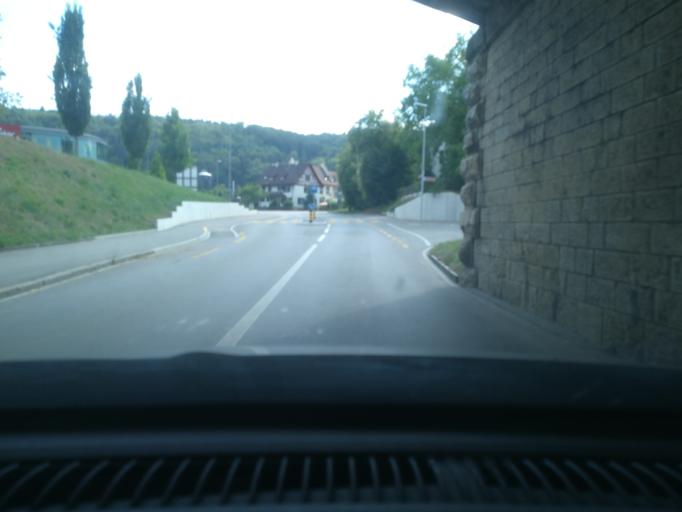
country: CH
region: Schaffhausen
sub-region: Bezirk Reiat
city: Thayngen
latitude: 47.7454
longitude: 8.7059
